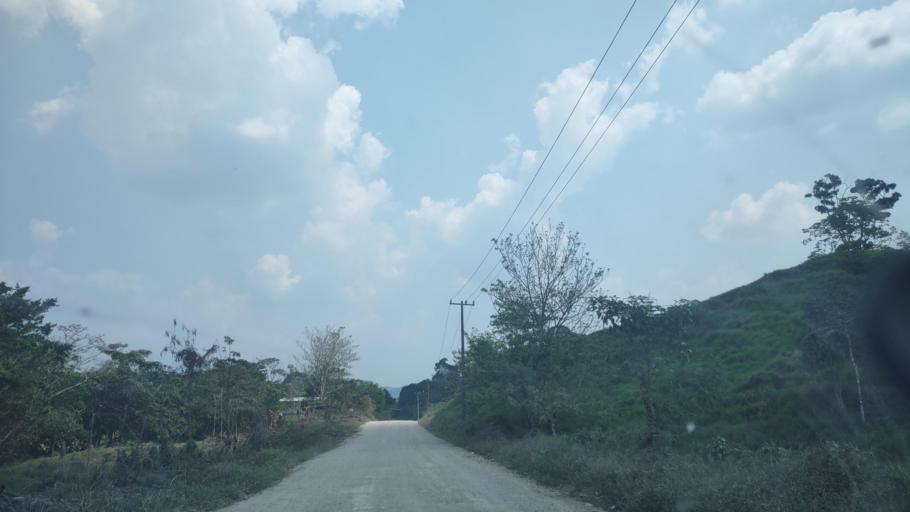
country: MX
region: Tabasco
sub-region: Huimanguillo
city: Francisco Rueda
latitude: 17.5962
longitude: -93.8995
